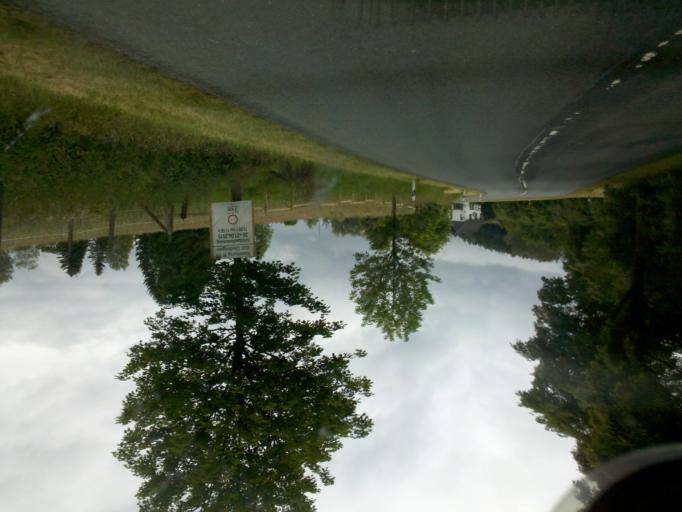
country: DE
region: North Rhine-Westphalia
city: Eslohe
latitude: 51.1930
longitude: 8.1443
